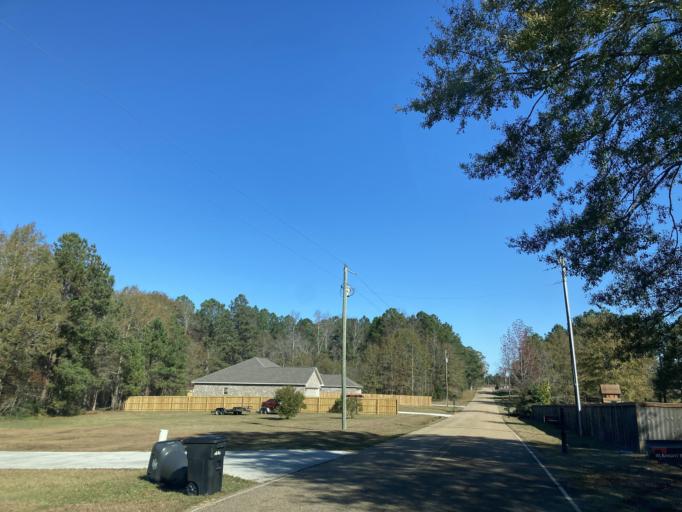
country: US
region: Mississippi
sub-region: Lamar County
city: Sumrall
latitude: 31.2598
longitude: -89.5391
